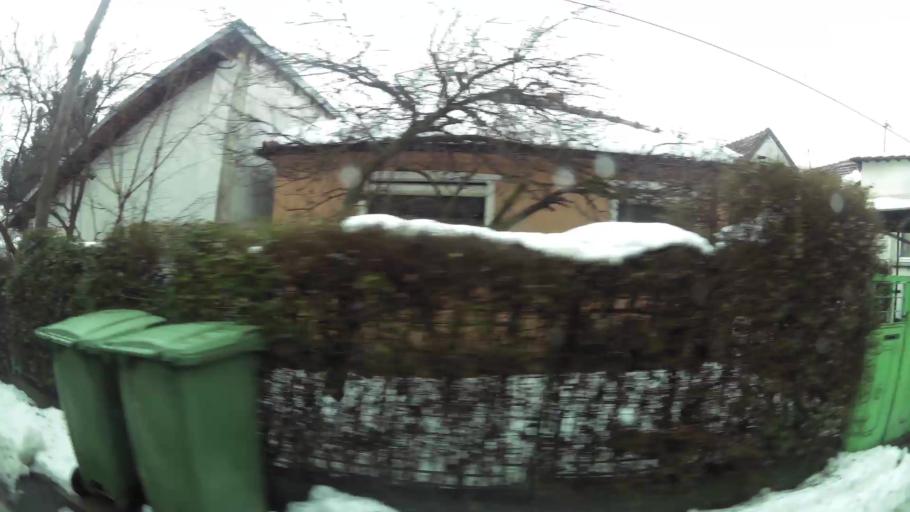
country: RS
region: Central Serbia
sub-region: Belgrade
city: Zvezdara
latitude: 44.7812
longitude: 20.5206
